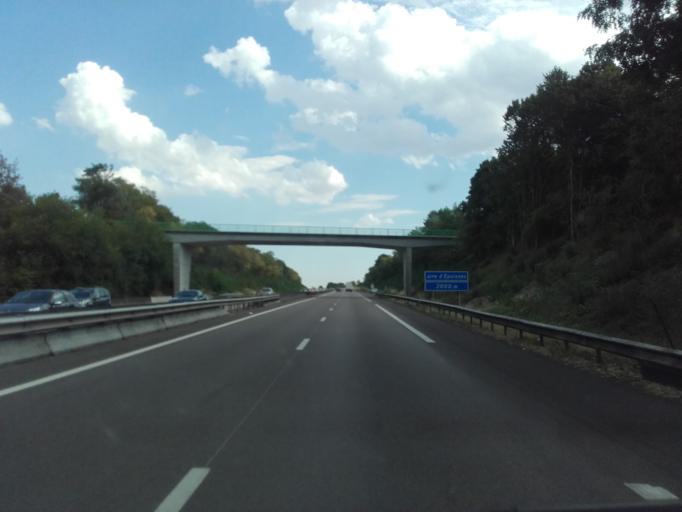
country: FR
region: Bourgogne
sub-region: Departement de la Cote-d'Or
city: Semur-en-Auxois
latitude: 47.4931
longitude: 4.1276
